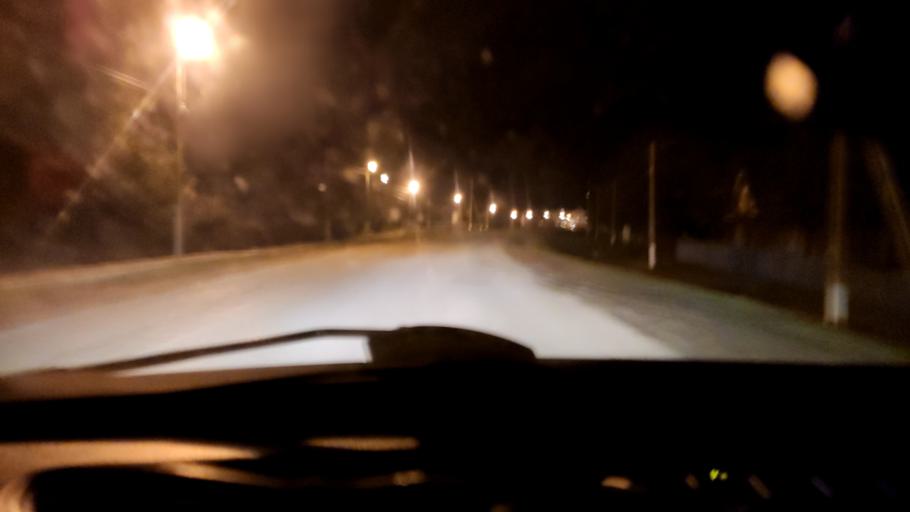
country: RU
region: Bashkortostan
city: Karmaskaly
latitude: 54.3620
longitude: 56.1665
